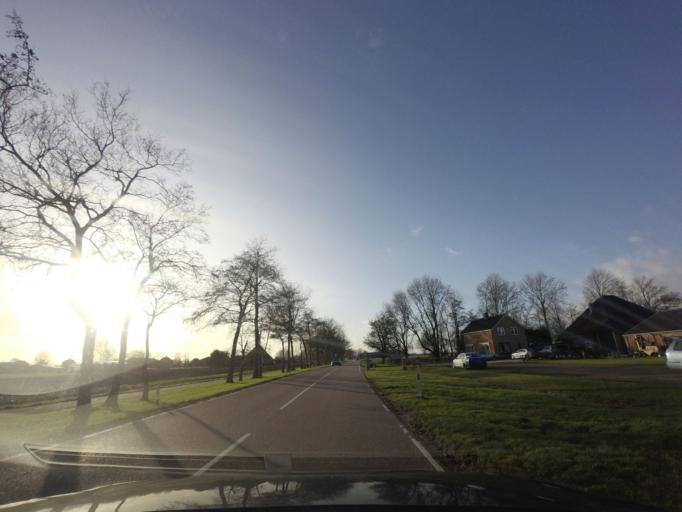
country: NL
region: North Holland
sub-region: Gemeente Schagen
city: Schagen
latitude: 52.7464
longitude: 4.8516
